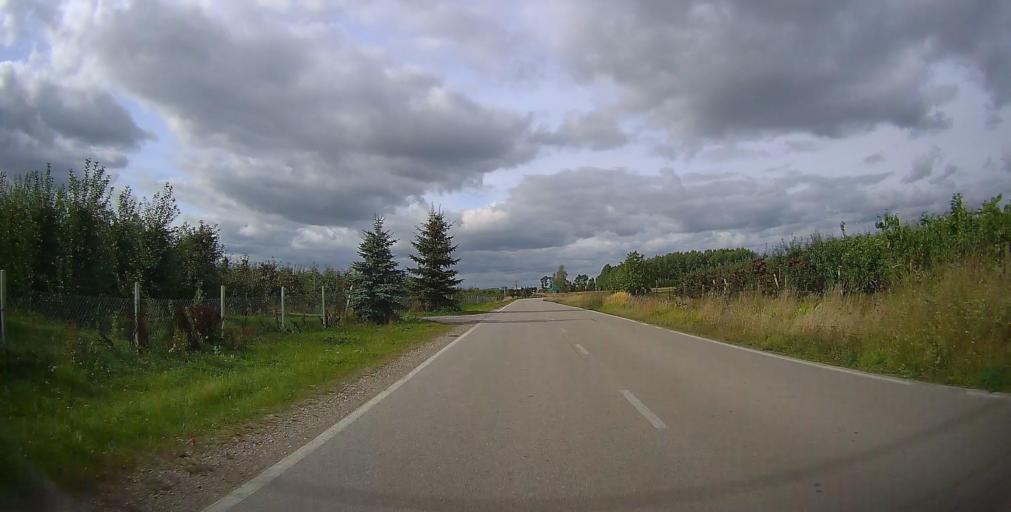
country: PL
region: Masovian Voivodeship
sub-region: Powiat grojecki
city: Goszczyn
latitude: 51.7588
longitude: 20.9015
